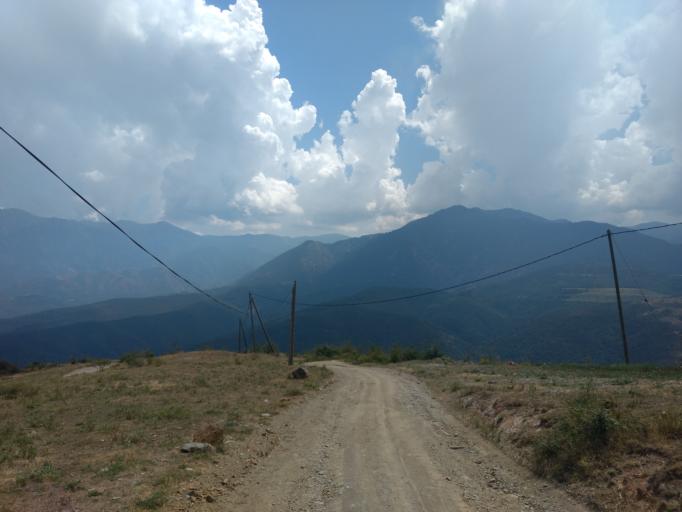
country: FR
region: Languedoc-Roussillon
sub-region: Departement des Pyrenees-Orientales
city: Vernet-les-Bains
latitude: 42.5734
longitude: 2.2910
